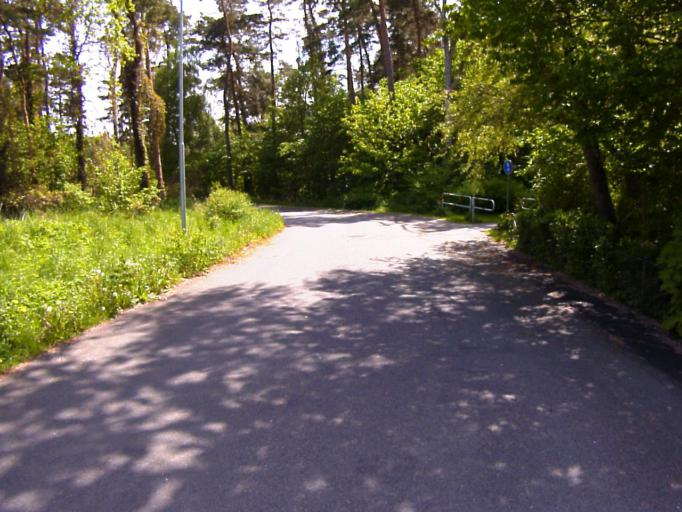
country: SE
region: Skane
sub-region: Kristianstads Kommun
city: Kristianstad
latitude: 56.0699
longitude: 14.0890
